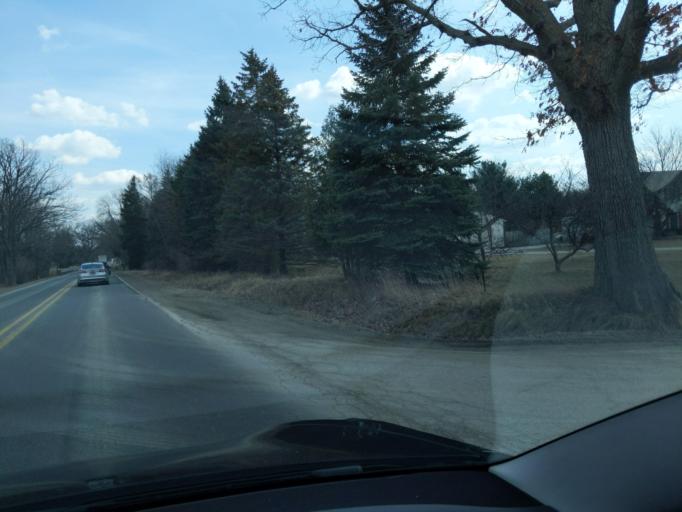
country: US
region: Michigan
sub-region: Livingston County
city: Whitmore Lake
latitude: 42.3806
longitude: -83.8062
